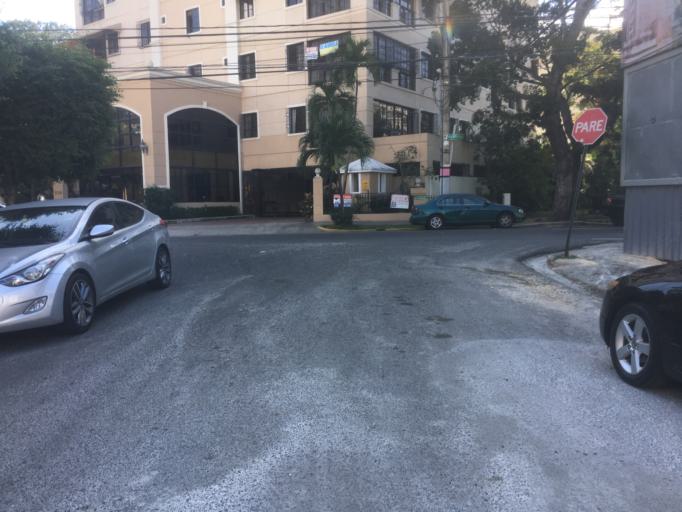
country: DO
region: Nacional
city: La Julia
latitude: 18.4699
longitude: -69.9199
